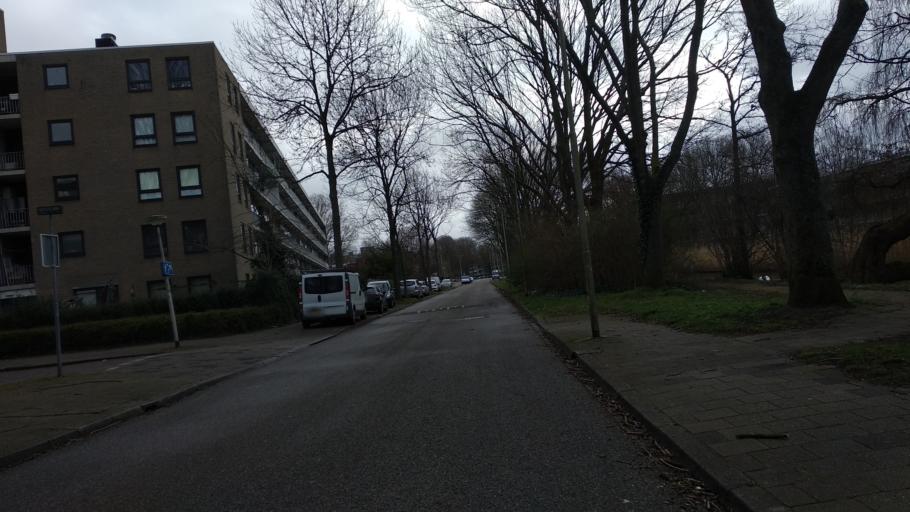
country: NL
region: South Holland
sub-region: Gemeente Delft
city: Delft
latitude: 51.9920
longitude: 4.3406
